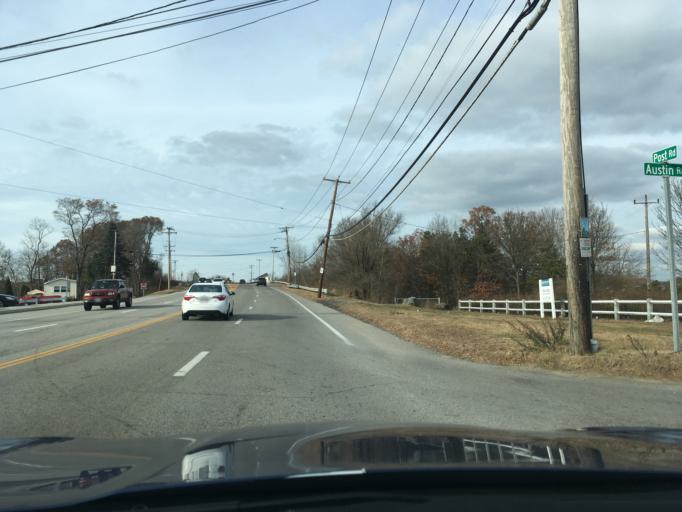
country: US
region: Rhode Island
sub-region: Kent County
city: East Greenwich
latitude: 41.6302
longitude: -71.4638
